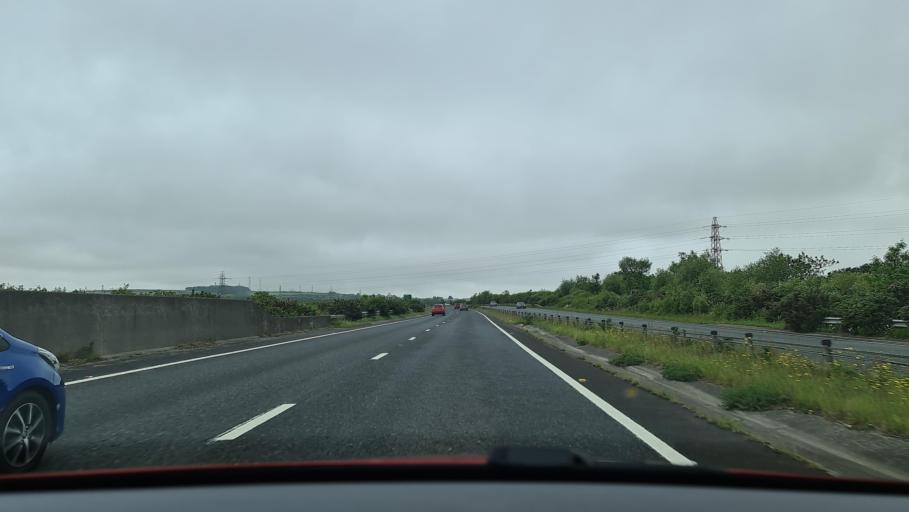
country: GB
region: England
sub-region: Cornwall
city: Saint Dennis
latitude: 50.4046
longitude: -4.9045
